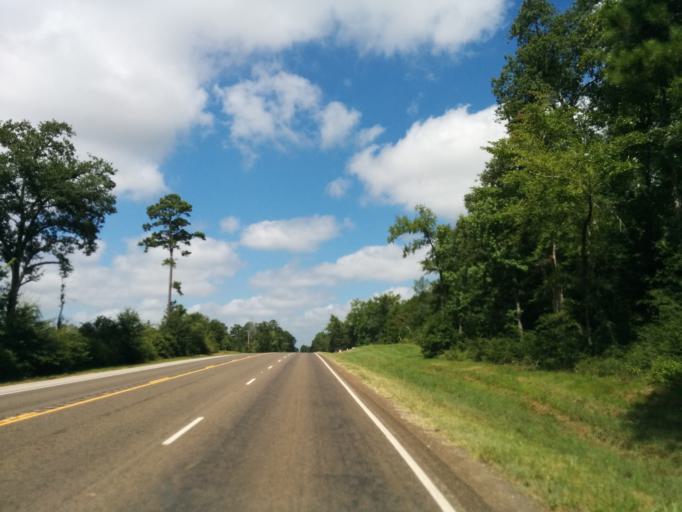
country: US
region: Texas
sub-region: Houston County
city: Hickory Creek
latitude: 31.3262
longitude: -95.3622
